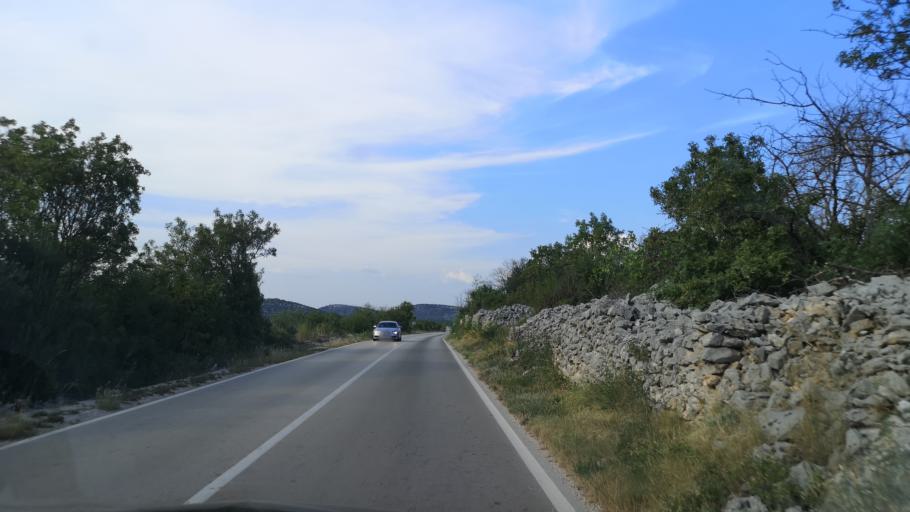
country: HR
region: Sibensko-Kniniska
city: Vodice
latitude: 43.8023
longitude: 15.7731
